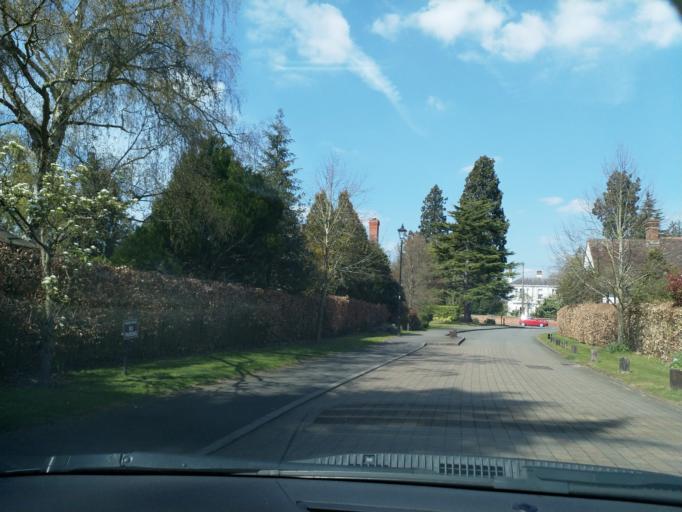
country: GB
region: England
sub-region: Warwickshire
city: Stratford-upon-Avon
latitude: 52.1940
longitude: -1.6916
